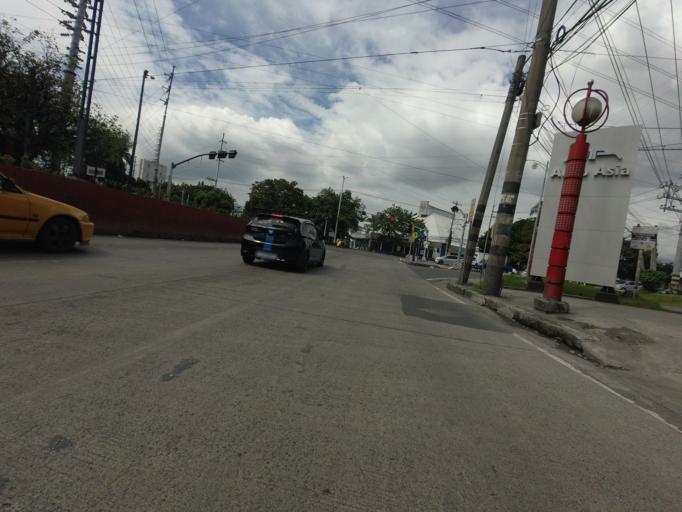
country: PH
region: Metro Manila
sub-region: City of Manila
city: Quiapo
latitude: 14.5853
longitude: 120.9941
